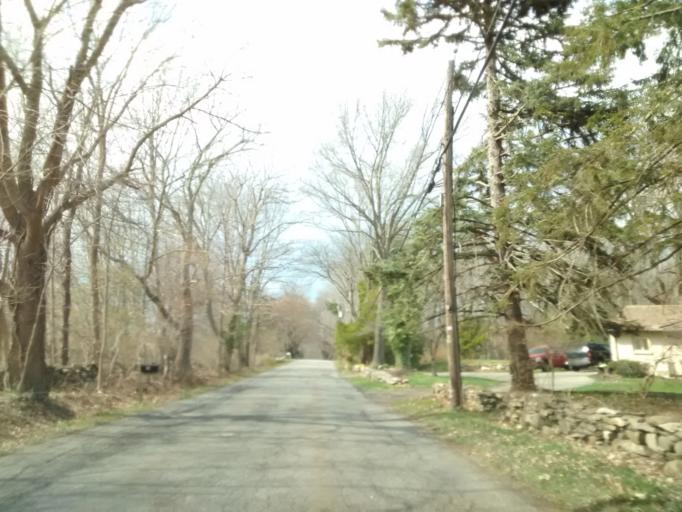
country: US
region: Massachusetts
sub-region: Worcester County
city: Sutton
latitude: 42.1377
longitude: -71.7862
